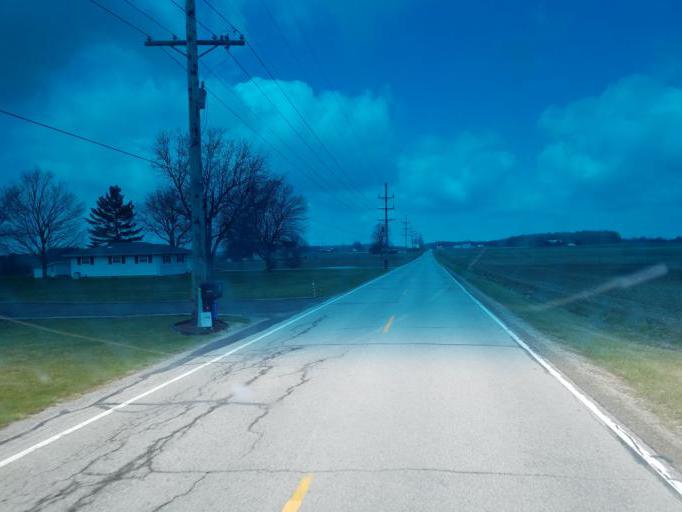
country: US
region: Ohio
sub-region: Crawford County
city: Galion
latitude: 40.7849
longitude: -82.8236
